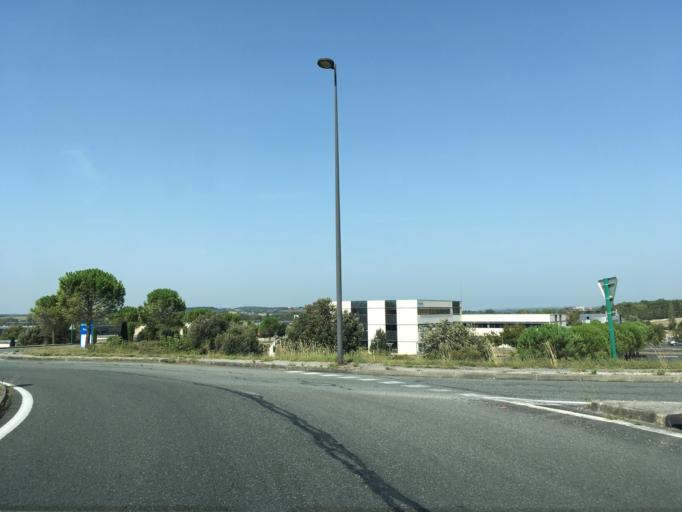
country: FR
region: Midi-Pyrenees
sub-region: Departement du Tarn
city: Lagarrigue
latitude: 43.5567
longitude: 2.2780
